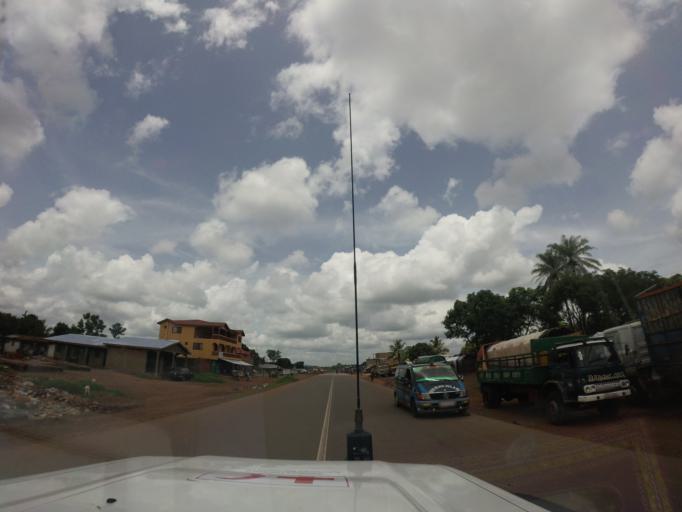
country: SL
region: Northern Province
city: Kambia
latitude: 9.0413
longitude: -12.9096
